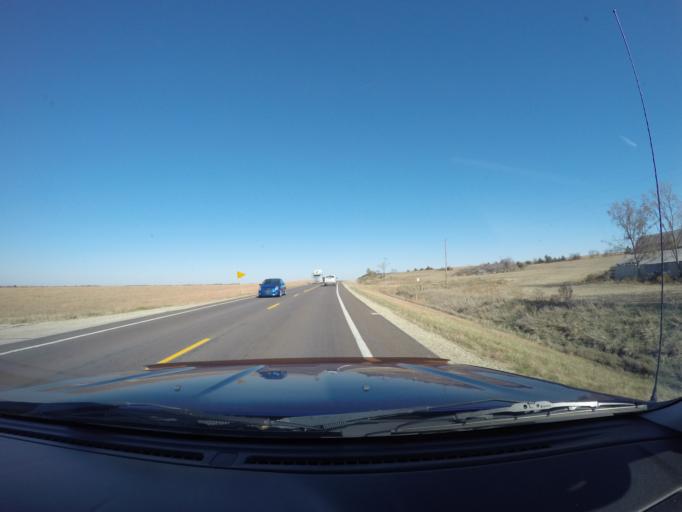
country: US
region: Kansas
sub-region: Marshall County
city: Blue Rapids
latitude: 39.5229
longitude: -96.7554
